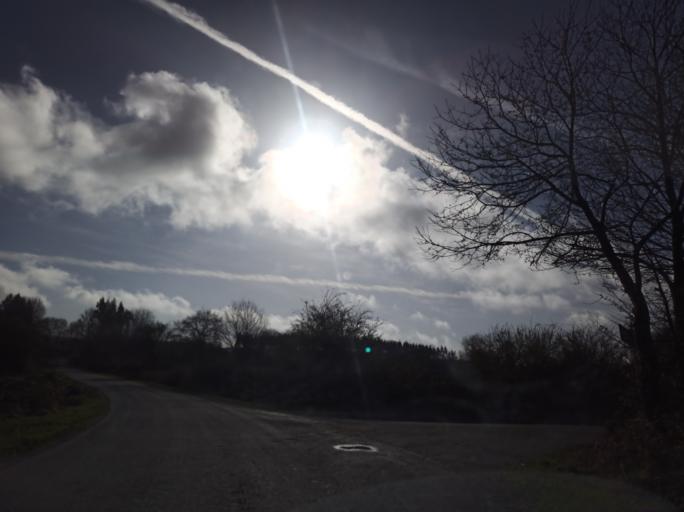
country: ES
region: Galicia
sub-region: Provincia da Coruna
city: Sobrado
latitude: 43.0856
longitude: -7.9655
